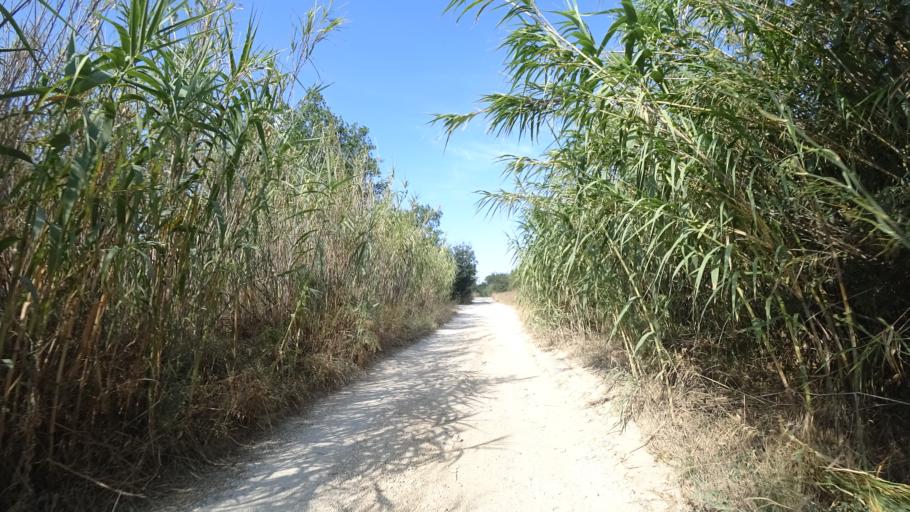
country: FR
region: Languedoc-Roussillon
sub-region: Departement des Pyrenees-Orientales
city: Rivesaltes
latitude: 42.7750
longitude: 2.8605
